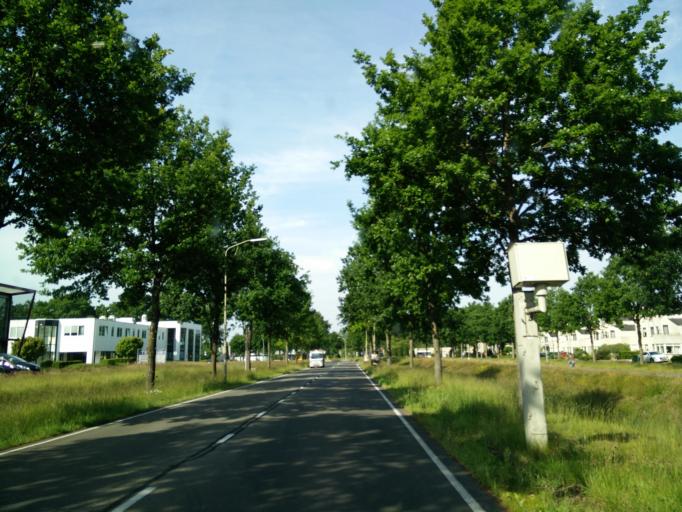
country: NL
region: Drenthe
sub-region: Gemeente Assen
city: Assen
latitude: 53.0138
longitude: 6.5799
